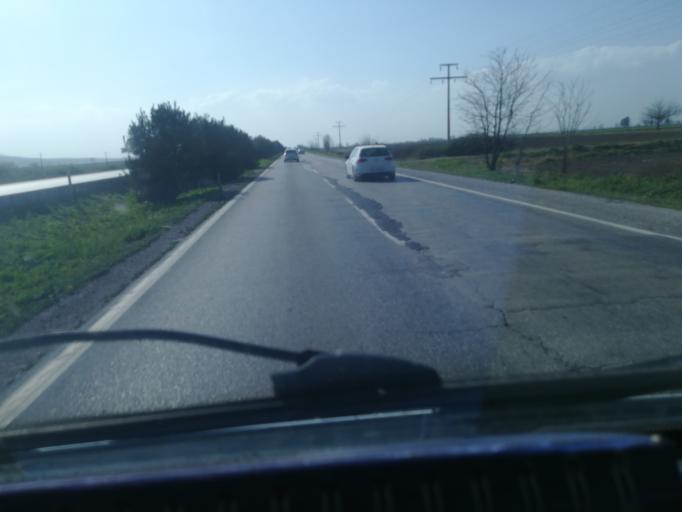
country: TR
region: Osmaniye
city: Toprakkale
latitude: 37.0744
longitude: 36.0568
